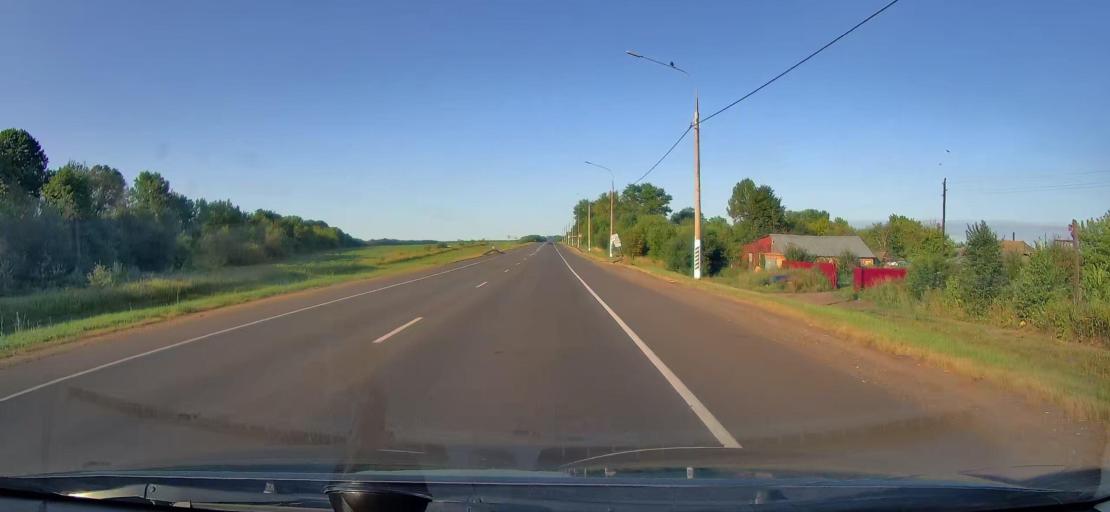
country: RU
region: Tula
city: Plavsk
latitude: 53.6487
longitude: 37.2239
